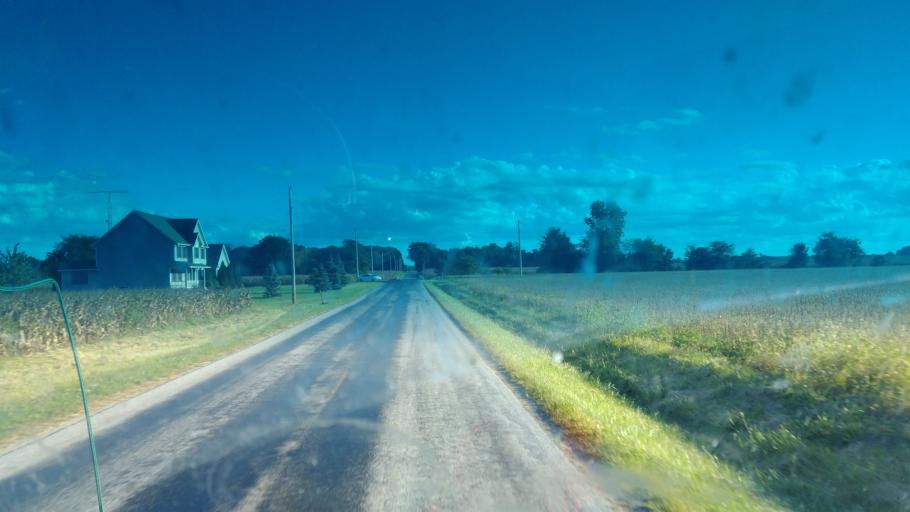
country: US
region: Ohio
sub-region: Wyandot County
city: Carey
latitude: 40.9210
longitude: -83.4009
